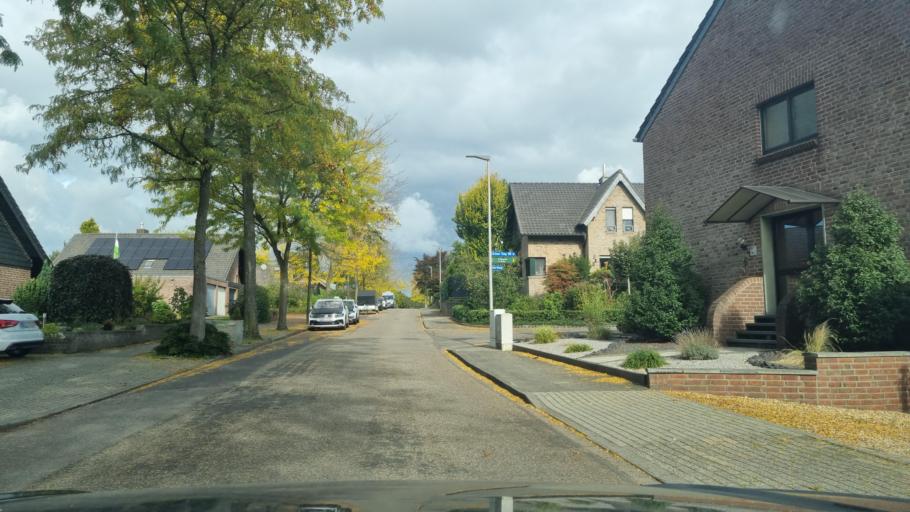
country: DE
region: North Rhine-Westphalia
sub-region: Regierungsbezirk Dusseldorf
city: Kleve
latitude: 51.7799
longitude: 6.1037
